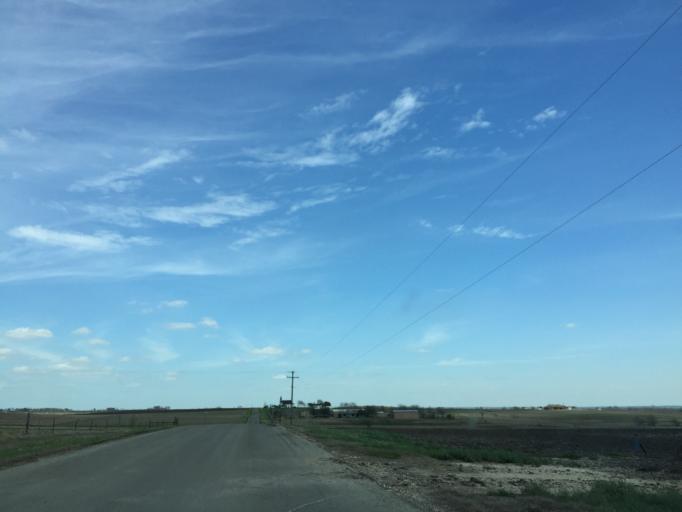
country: US
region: Texas
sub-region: Williamson County
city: Taylor
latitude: 30.5530
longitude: -97.3240
